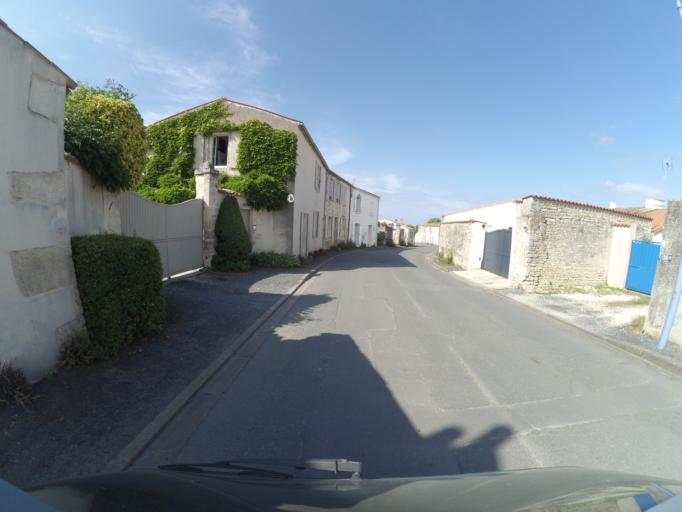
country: FR
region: Poitou-Charentes
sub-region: Departement de la Charente-Maritime
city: Andilly
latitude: 46.2418
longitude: -1.0663
